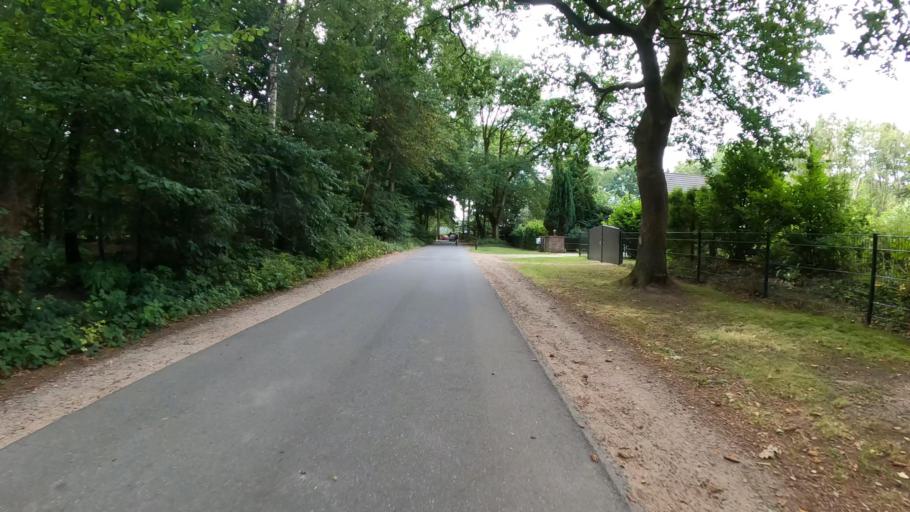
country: DE
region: Lower Saxony
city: Wenzendorf
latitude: 53.3613
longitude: 9.7557
